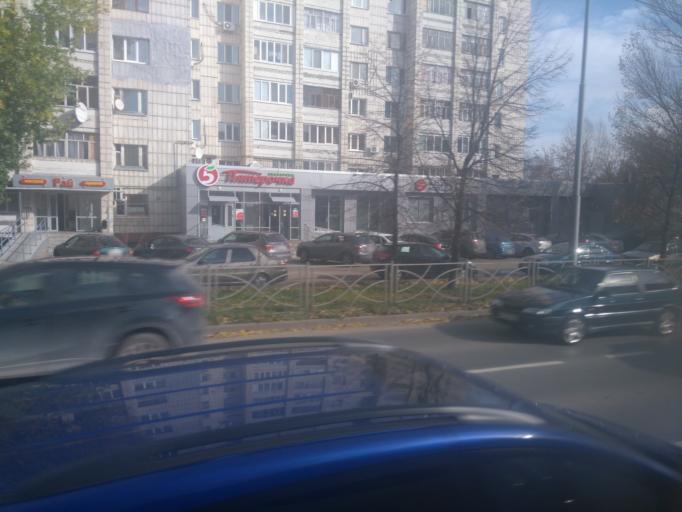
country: RU
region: Tatarstan
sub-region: Gorod Kazan'
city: Kazan
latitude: 55.7974
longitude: 49.1933
